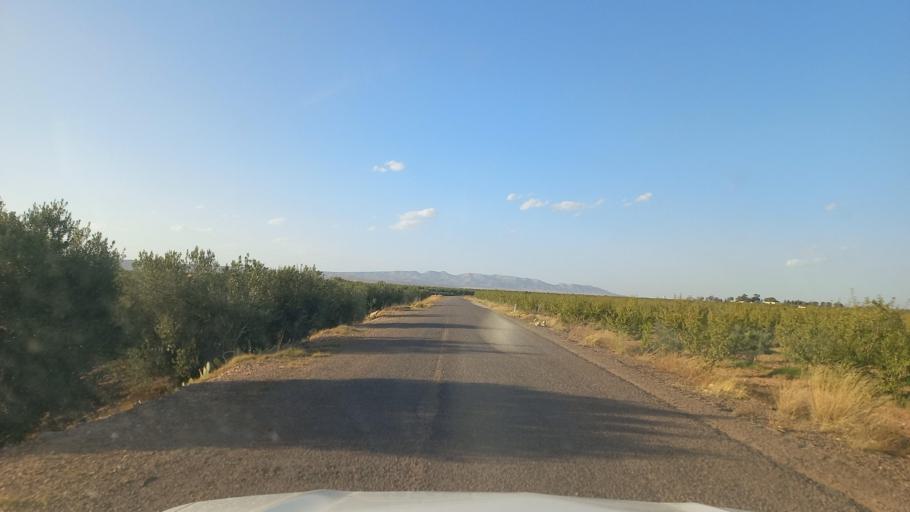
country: TN
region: Al Qasrayn
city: Kasserine
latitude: 35.2839
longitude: 9.0271
